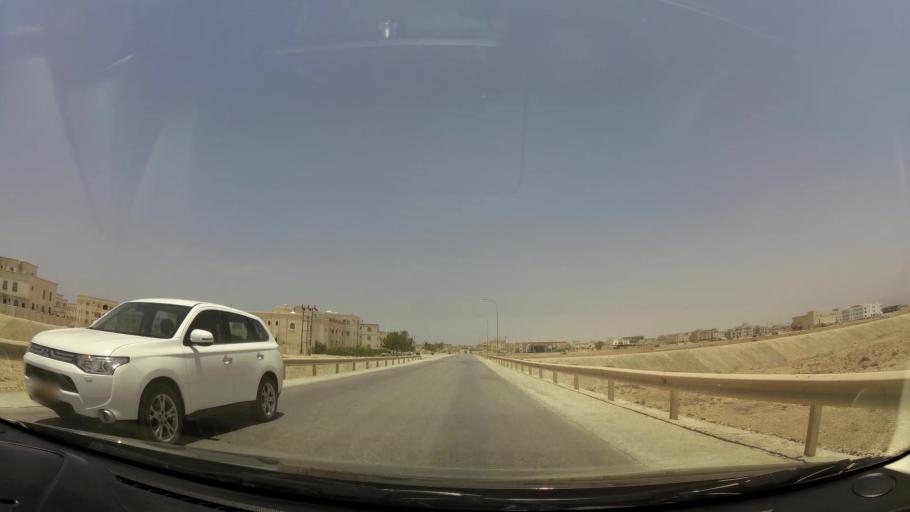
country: OM
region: Zufar
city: Salalah
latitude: 17.0839
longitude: 54.1607
